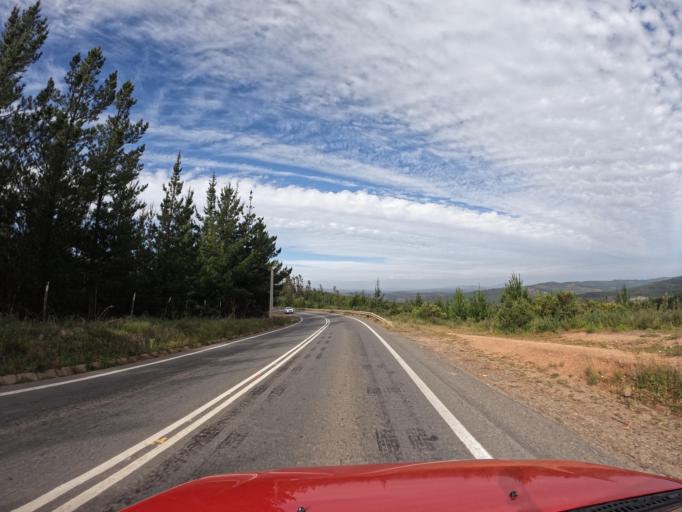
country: CL
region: O'Higgins
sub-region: Provincia de Colchagua
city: Santa Cruz
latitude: -34.3096
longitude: -71.8404
